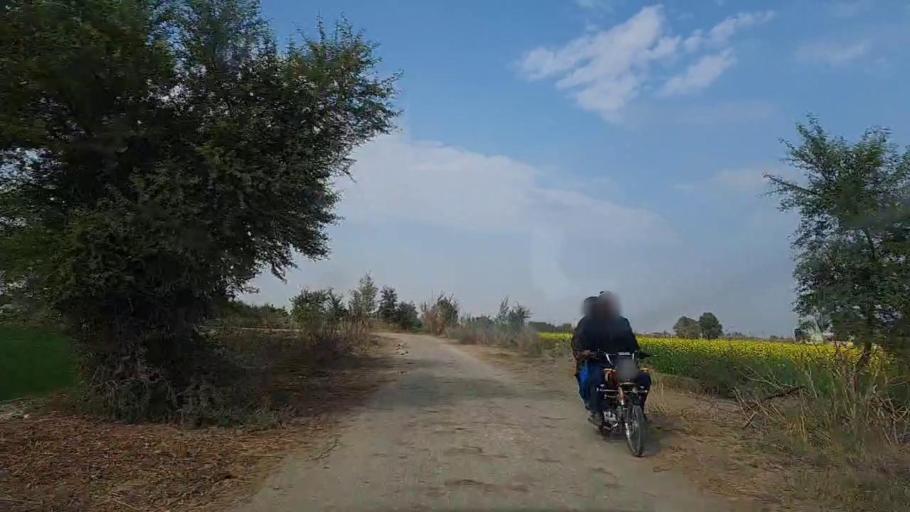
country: PK
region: Sindh
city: Sanghar
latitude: 26.2396
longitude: 69.0199
